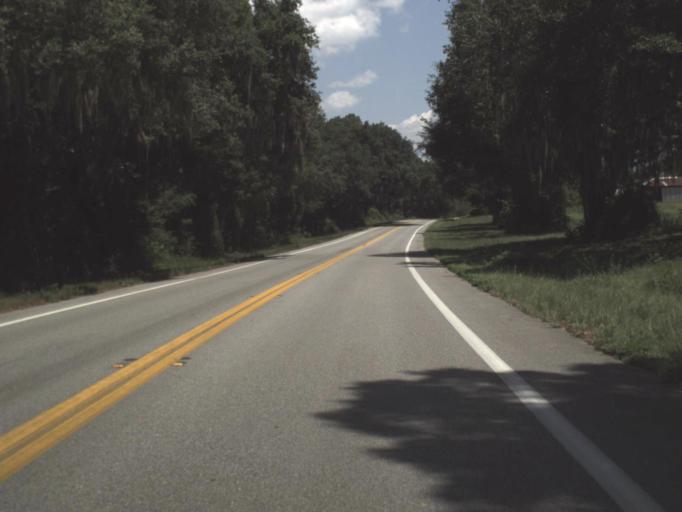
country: US
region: Florida
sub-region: Madison County
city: Madison
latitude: 30.5214
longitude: -83.6330
